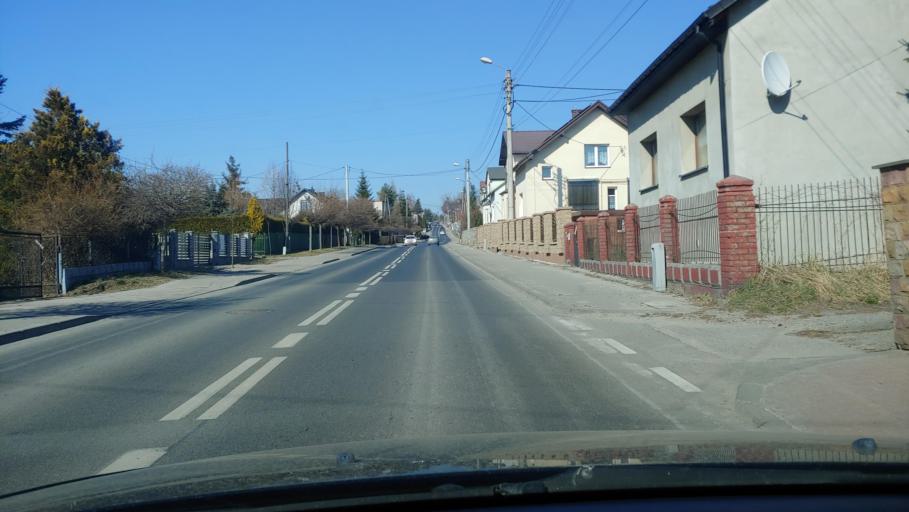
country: PL
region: Lesser Poland Voivodeship
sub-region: Powiat chrzanowski
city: Trzebinia
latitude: 50.1691
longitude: 19.4726
